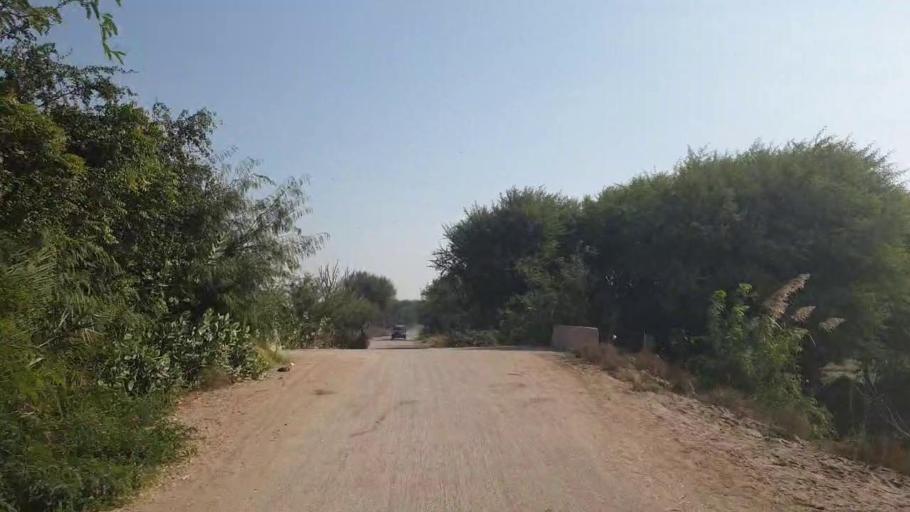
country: PK
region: Sindh
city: Matiari
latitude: 25.6766
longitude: 68.3518
